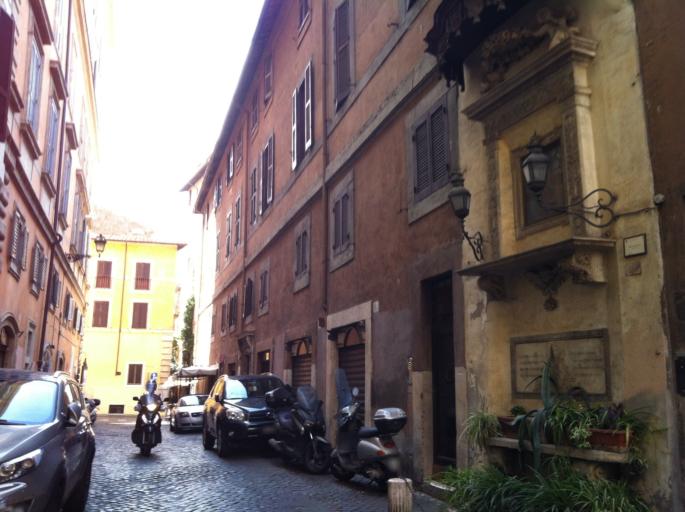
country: VA
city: Vatican City
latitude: 41.8969
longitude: 12.4770
